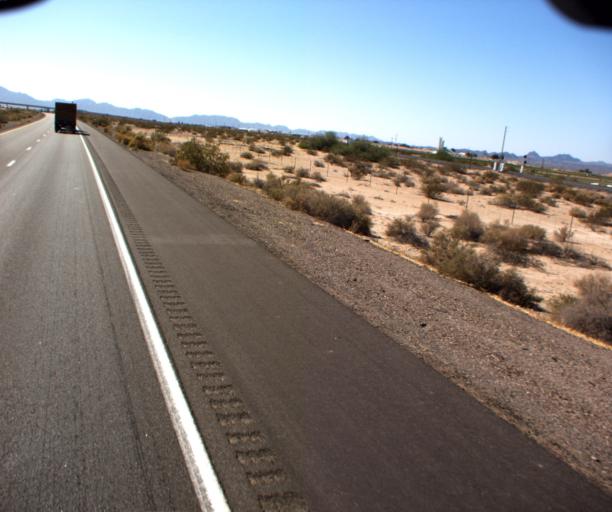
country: US
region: Arizona
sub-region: Yuma County
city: Wellton
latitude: 32.6721
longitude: -114.0989
